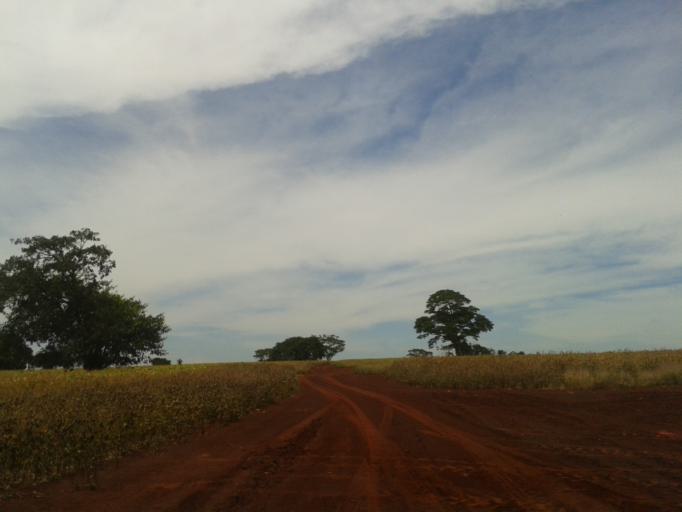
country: BR
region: Minas Gerais
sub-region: Capinopolis
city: Capinopolis
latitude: -18.6466
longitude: -49.7584
